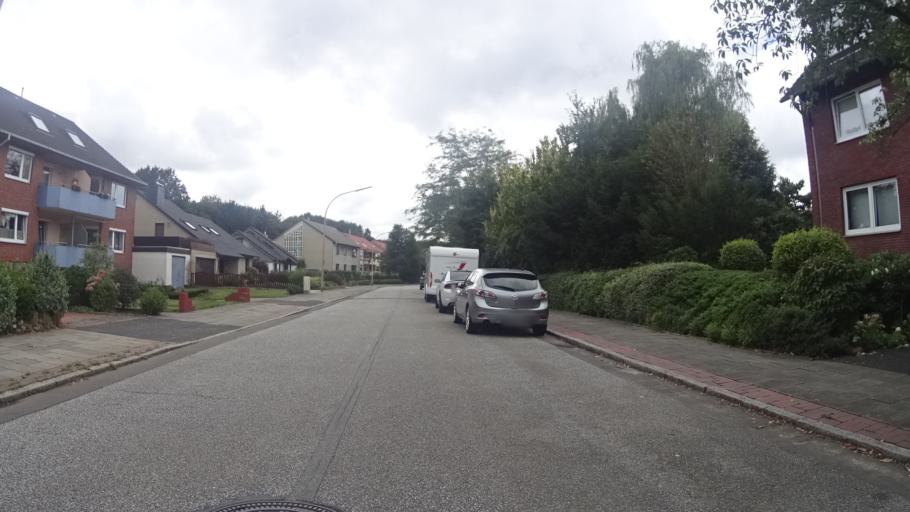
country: DE
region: Bremen
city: Bremerhaven
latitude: 53.5325
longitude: 8.6108
